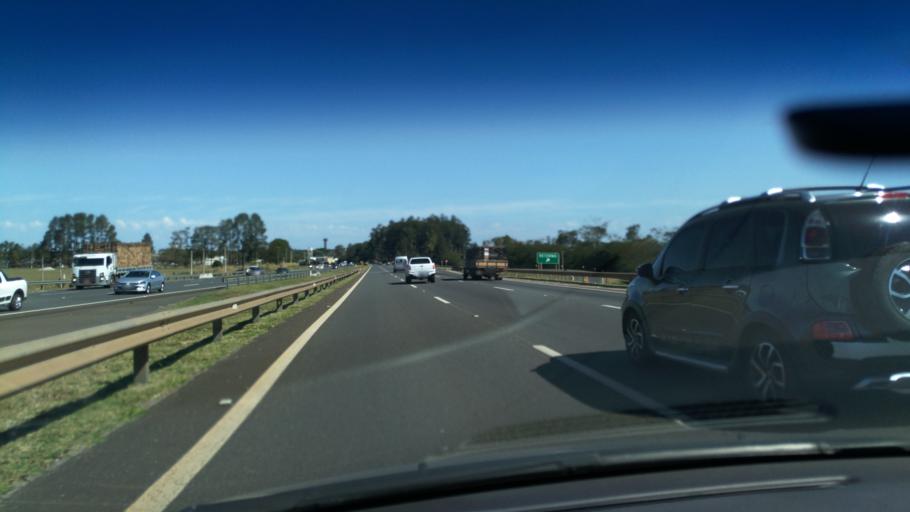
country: BR
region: Sao Paulo
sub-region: Jaguariuna
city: Jaguariuna
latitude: -22.7838
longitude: -47.0277
